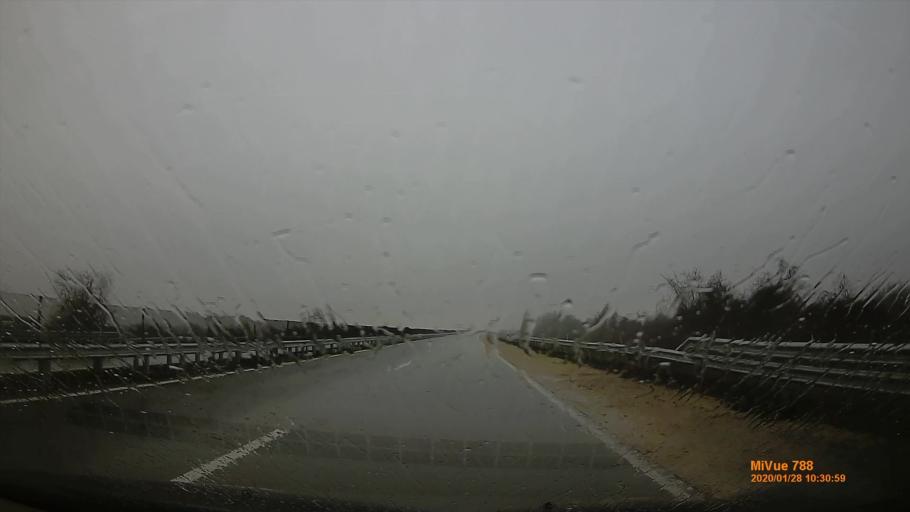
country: HU
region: Pest
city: Gomba
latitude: 47.3358
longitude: 19.5098
